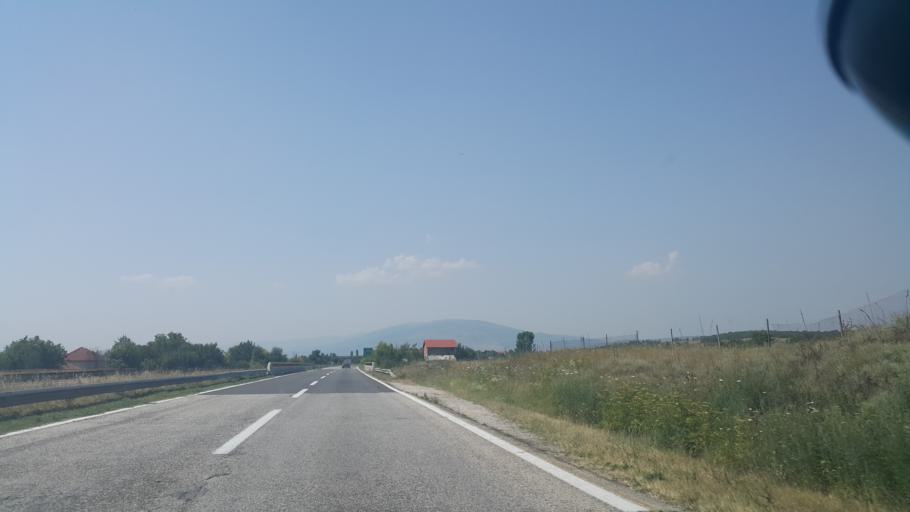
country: MK
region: Petrovec
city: Petrovec
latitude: 41.9217
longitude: 21.6358
